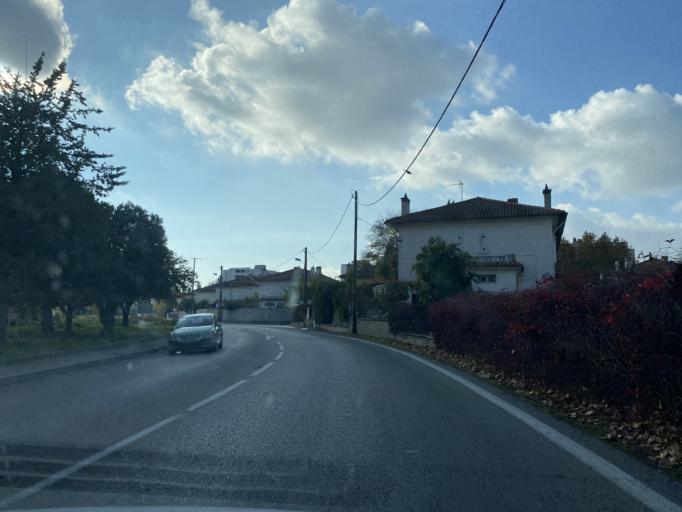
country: FR
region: Provence-Alpes-Cote d'Azur
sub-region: Departement du Var
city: La Seyne-sur-Mer
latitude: 43.1145
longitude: 5.8698
